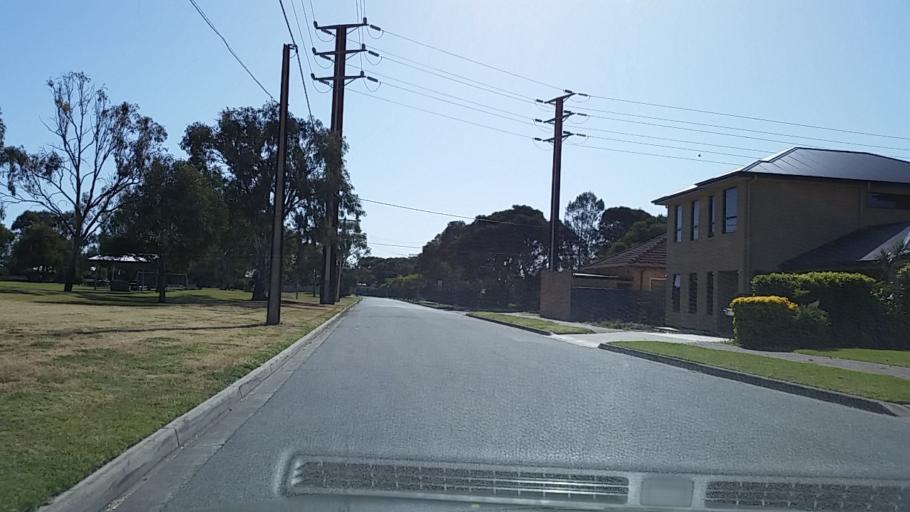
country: AU
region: South Australia
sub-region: Charles Sturt
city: Henley Beach
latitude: -34.9170
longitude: 138.5057
